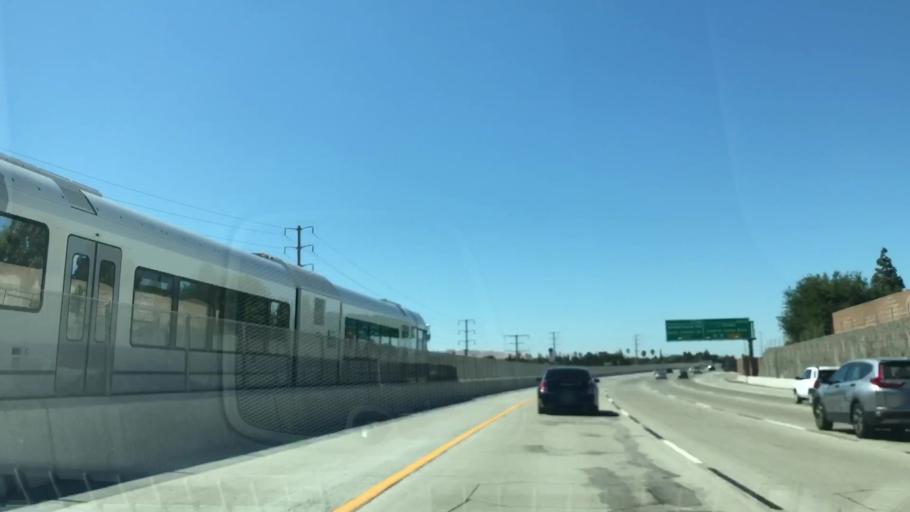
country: US
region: California
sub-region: Contra Costa County
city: Antioch
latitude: 37.9984
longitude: -121.8162
